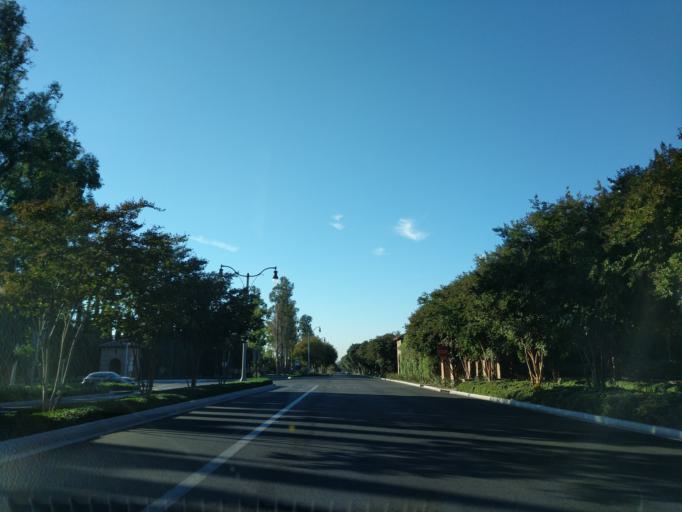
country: US
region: California
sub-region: Orange County
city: Irvine
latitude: 33.6932
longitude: -117.7504
